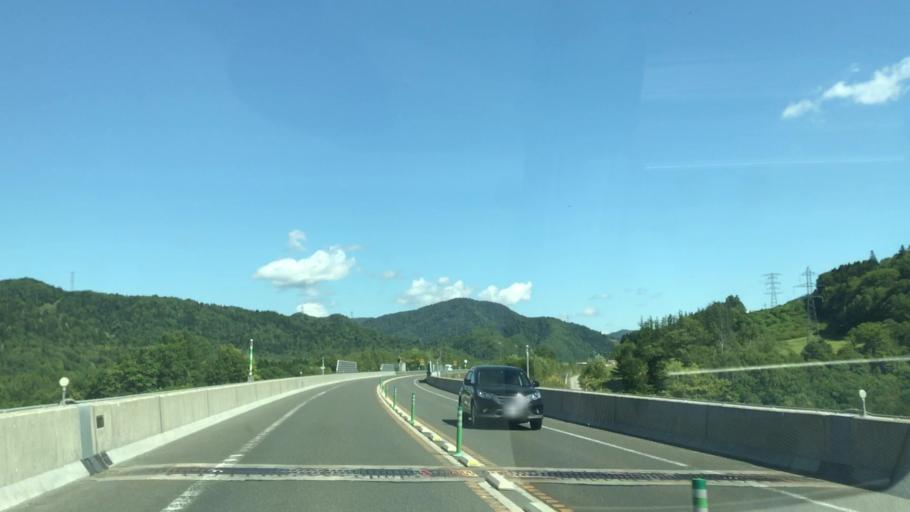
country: JP
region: Hokkaido
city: Shimo-furano
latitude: 43.0018
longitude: 142.4114
